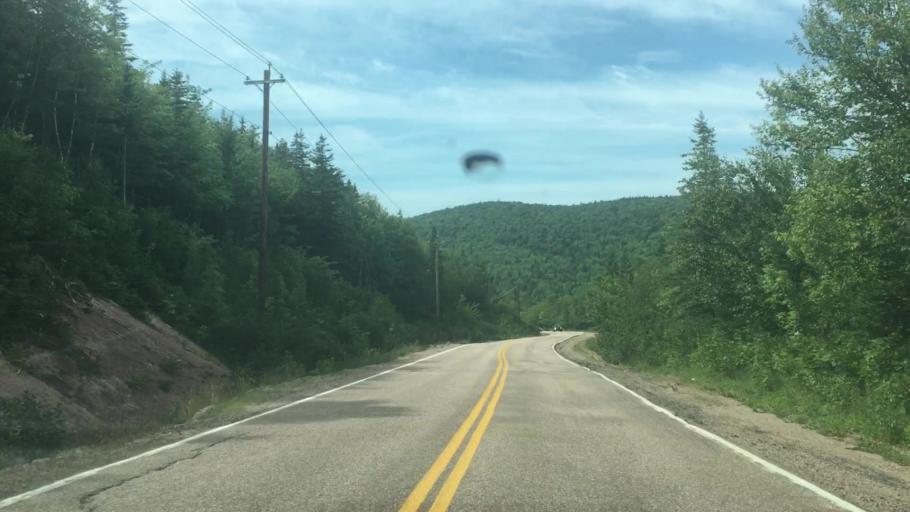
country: CA
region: Nova Scotia
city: Sydney Mines
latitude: 46.6048
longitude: -60.3892
